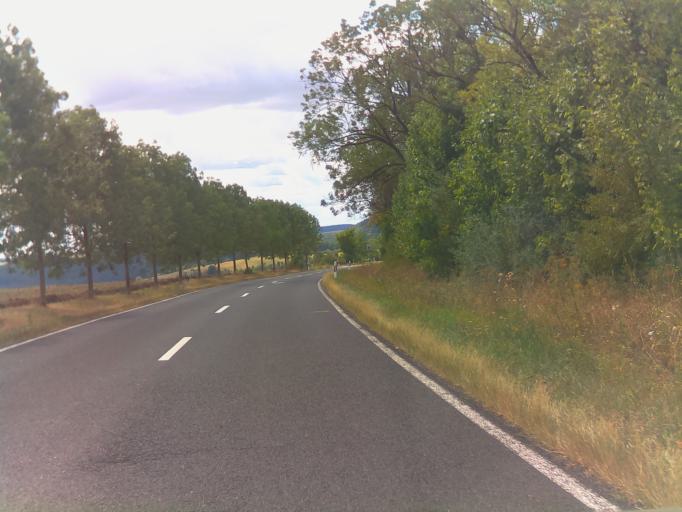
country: DE
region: Thuringia
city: Marisfeld
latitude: 50.5461
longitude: 10.5546
